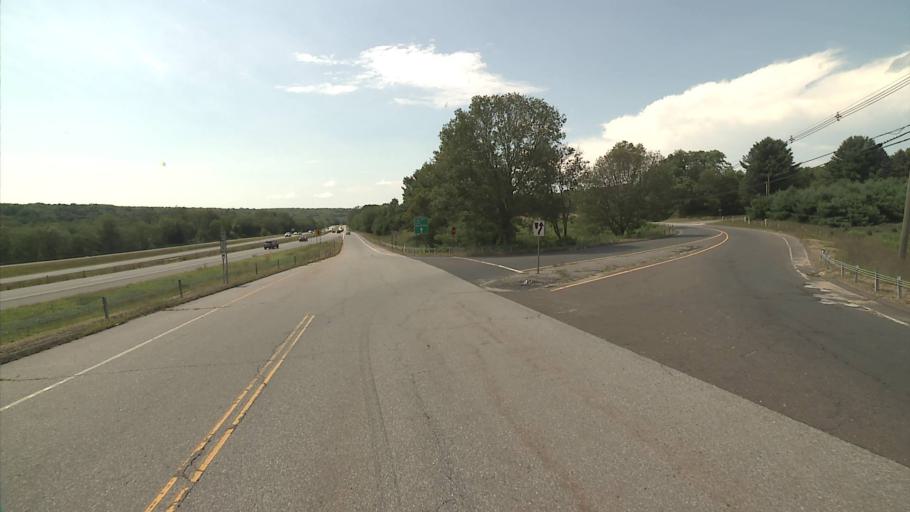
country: US
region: Connecticut
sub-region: New London County
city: Colchester
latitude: 41.5829
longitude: -72.3605
